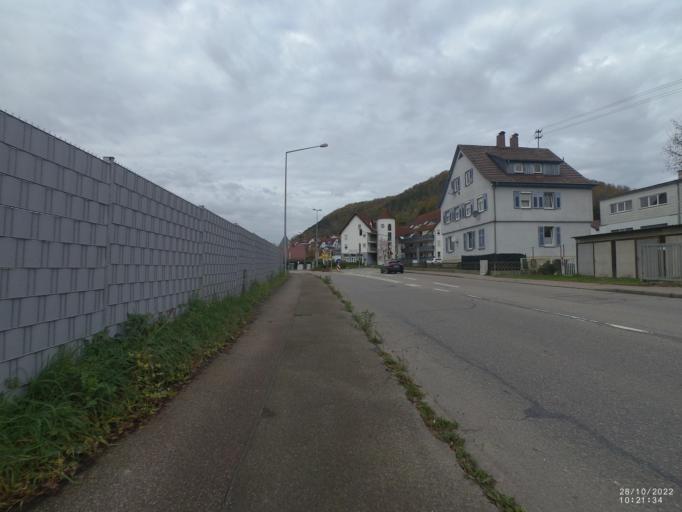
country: DE
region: Baden-Wuerttemberg
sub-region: Regierungsbezirk Stuttgart
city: Geislingen an der Steige
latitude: 48.6295
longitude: 9.8426
